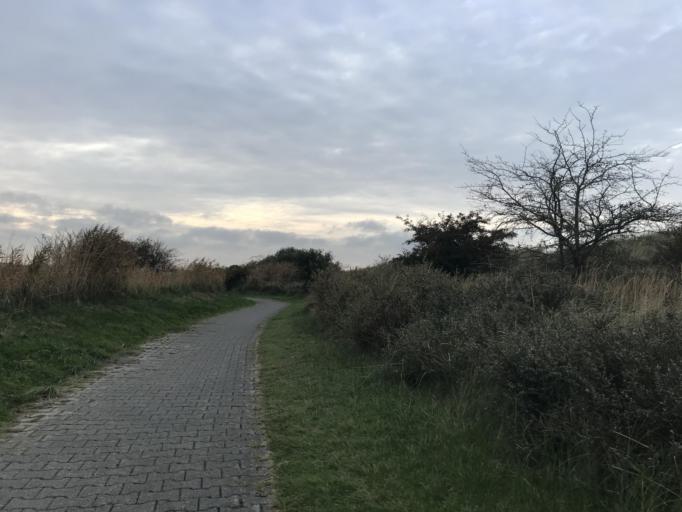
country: DE
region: Lower Saxony
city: Borkum
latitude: 53.6058
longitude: 6.7415
